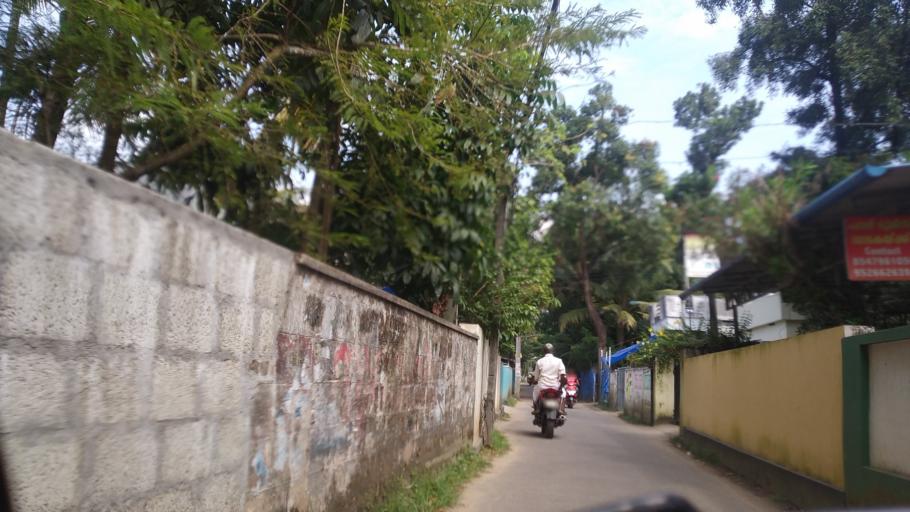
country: IN
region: Kerala
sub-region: Ernakulam
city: Elur
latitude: 10.0862
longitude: 76.2073
